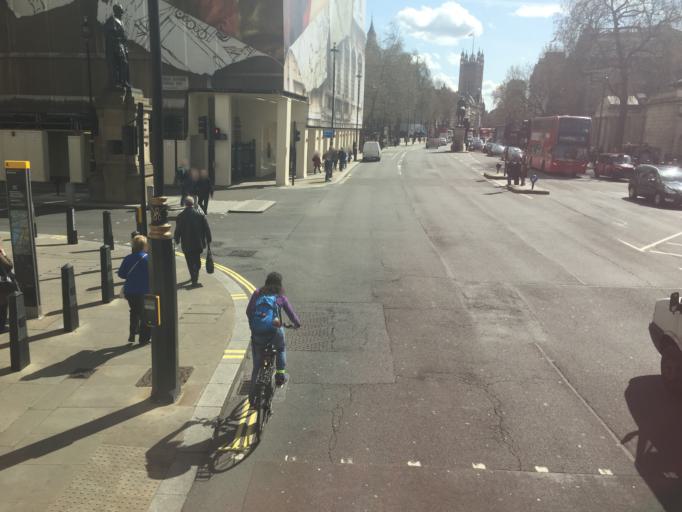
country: GB
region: England
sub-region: Greater London
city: London
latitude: 51.5050
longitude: -0.1264
